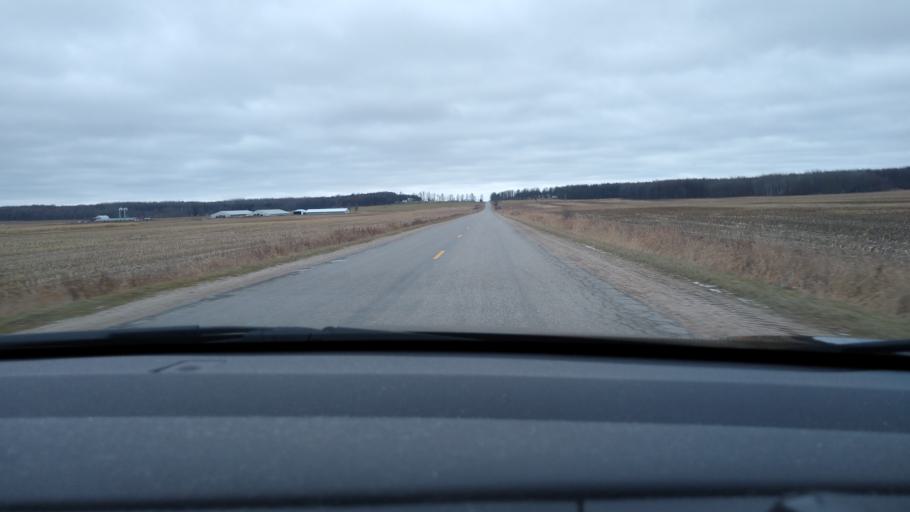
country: US
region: Michigan
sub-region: Missaukee County
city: Lake City
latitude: 44.3125
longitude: -85.0546
